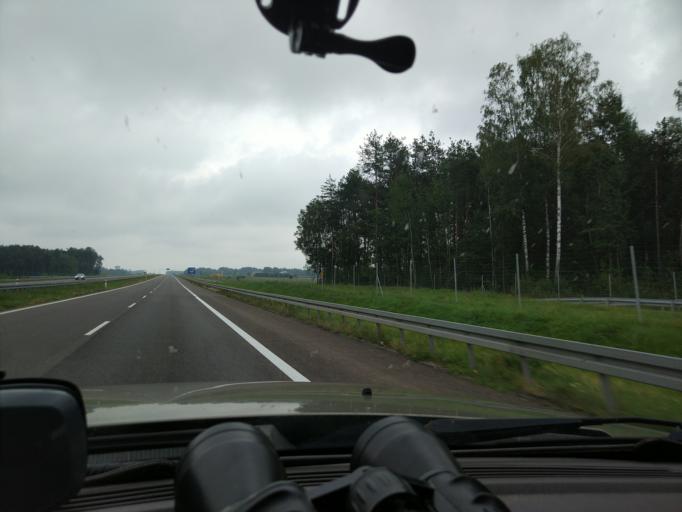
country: PL
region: Podlasie
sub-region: Powiat zambrowski
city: Zambrow
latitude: 53.0272
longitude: 22.3312
